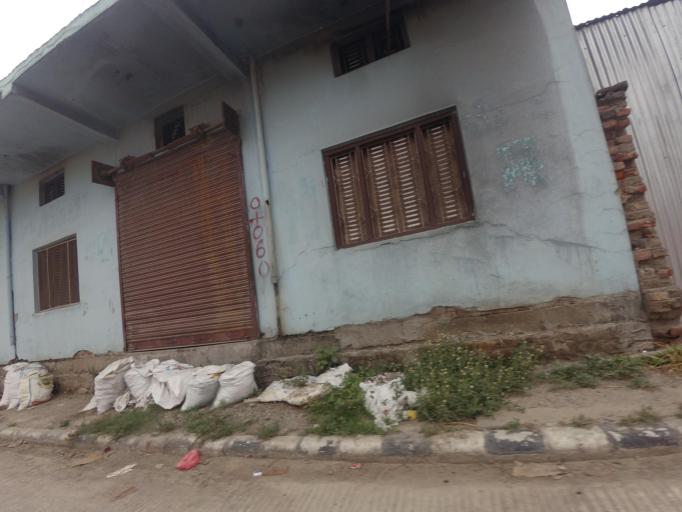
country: NP
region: Western Region
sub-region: Lumbini Zone
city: Bhairahawa
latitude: 27.5013
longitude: 83.4486
